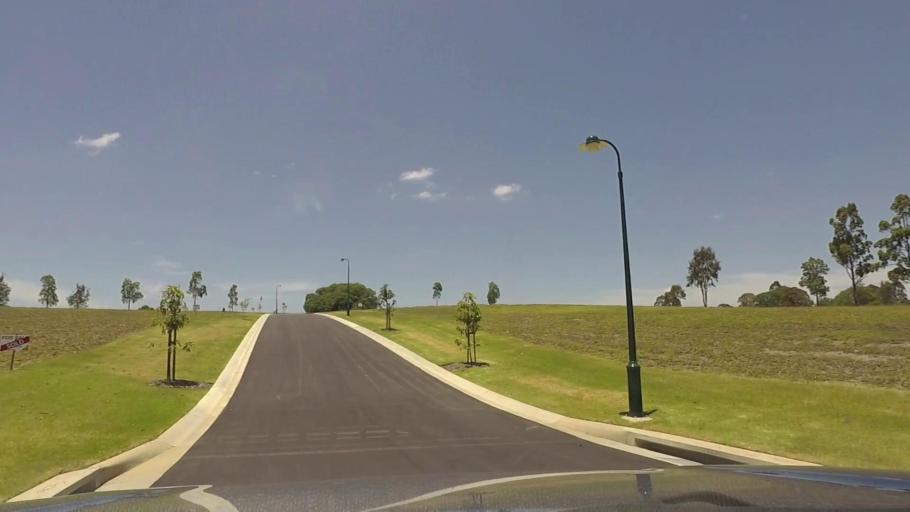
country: AU
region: Queensland
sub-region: Logan
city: Chambers Flat
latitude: -27.7725
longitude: 153.0870
